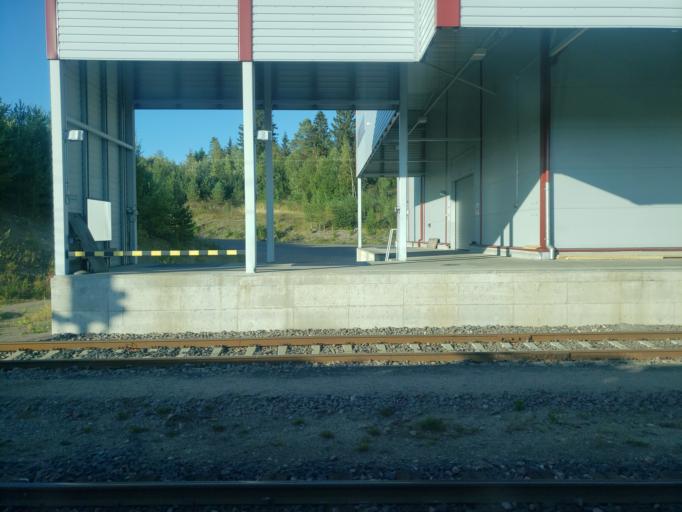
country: FI
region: South Karelia
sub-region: Lappeenranta
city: Lappeenranta
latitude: 60.8676
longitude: 28.2890
